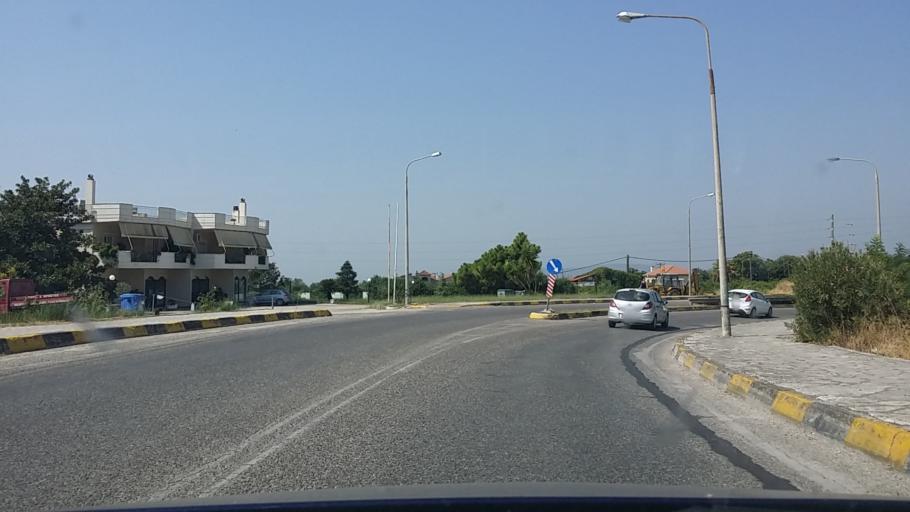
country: GR
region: Epirus
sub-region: Nomos Artas
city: Arta
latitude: 39.1506
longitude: 20.9746
